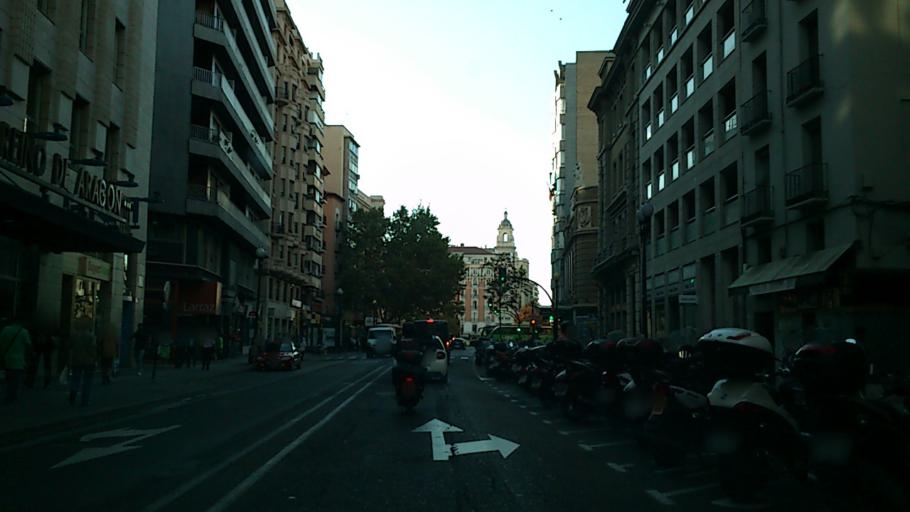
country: ES
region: Aragon
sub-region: Provincia de Zaragoza
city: Zaragoza
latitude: 41.6512
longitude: -0.8784
